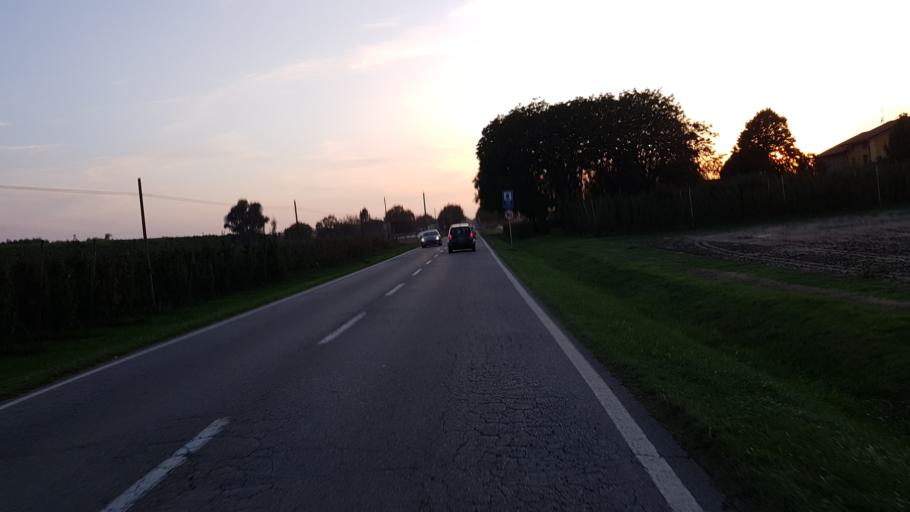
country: IT
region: Emilia-Romagna
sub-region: Provincia di Modena
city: Camposanto
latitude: 44.7924
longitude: 11.1662
